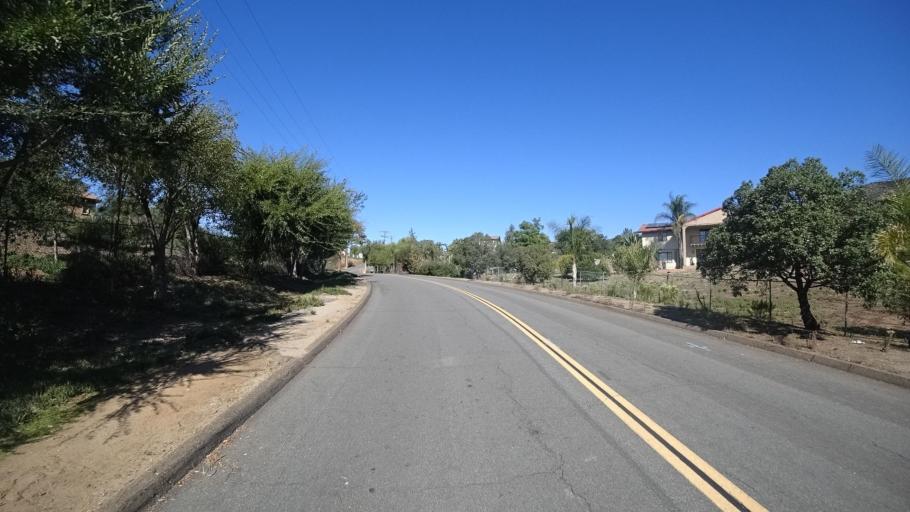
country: US
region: California
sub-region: San Diego County
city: Jamul
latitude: 32.7339
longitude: -116.8528
